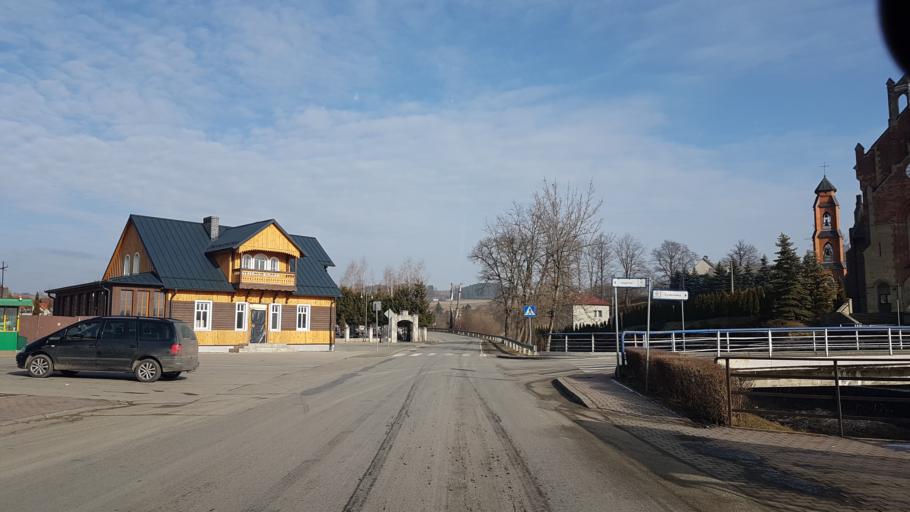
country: PL
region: Lesser Poland Voivodeship
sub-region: Powiat limanowski
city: Lukowica
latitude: 49.6410
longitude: 20.5037
